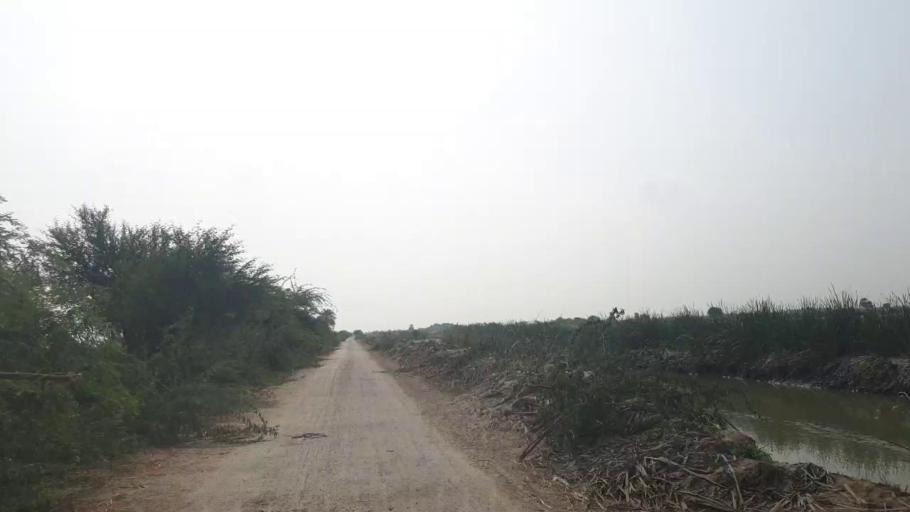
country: PK
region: Sindh
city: Badin
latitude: 24.7265
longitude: 68.7347
